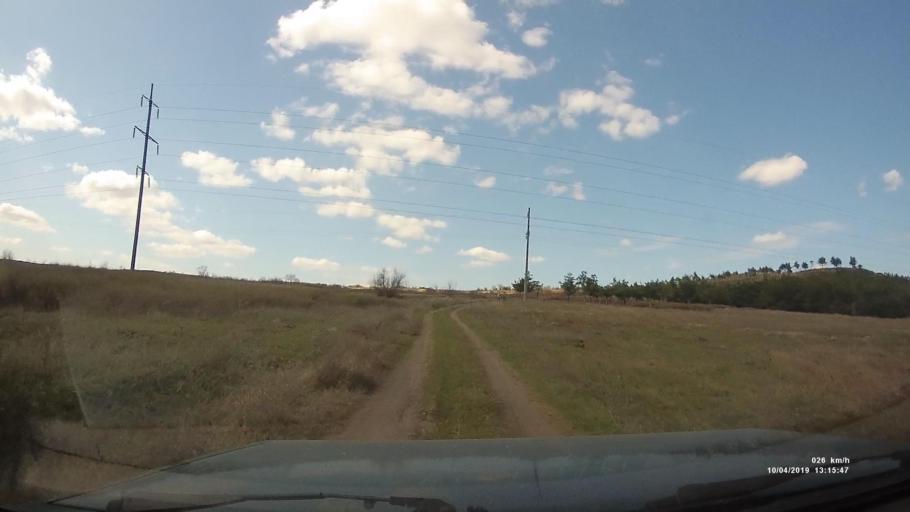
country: RU
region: Rostov
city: Masalovka
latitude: 48.4187
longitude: 40.2580
